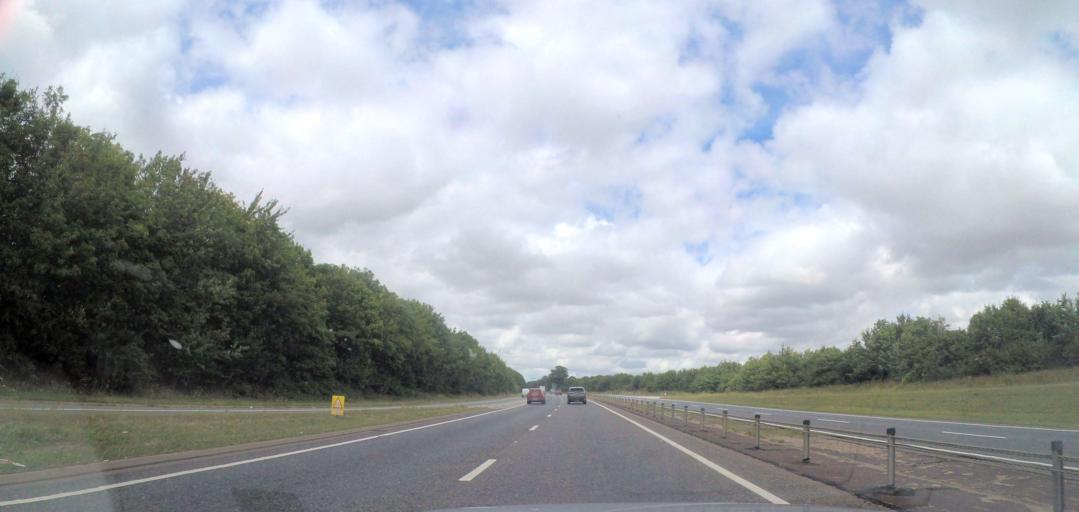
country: GB
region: England
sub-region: Cambridgeshire
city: Fulbourn
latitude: 52.1312
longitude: 0.2243
